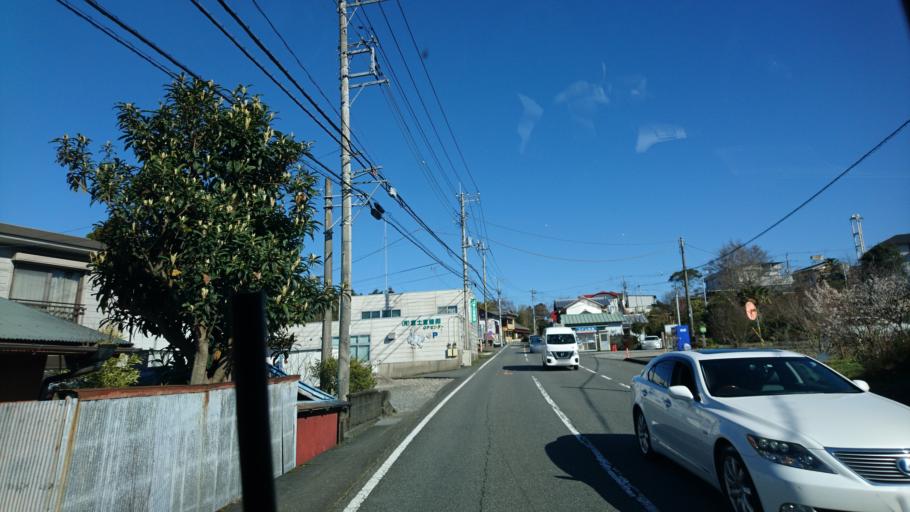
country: JP
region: Shizuoka
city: Fujinomiya
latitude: 35.2843
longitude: 138.6025
